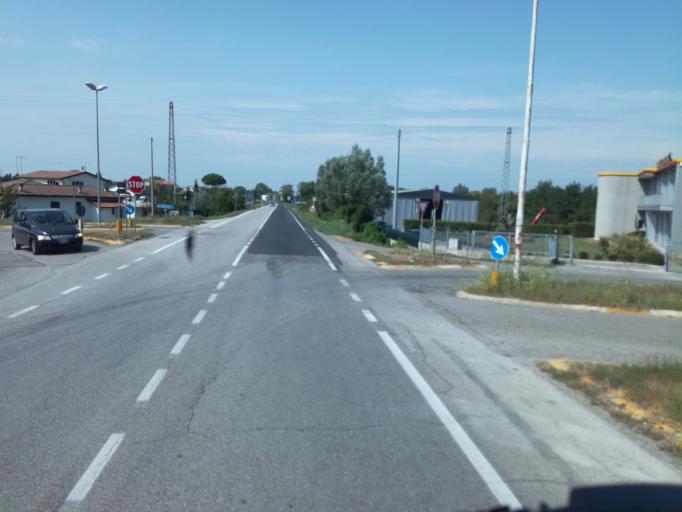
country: IT
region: Veneto
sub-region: Provincia di Rovigo
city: Loreo
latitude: 45.0601
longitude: 12.1852
